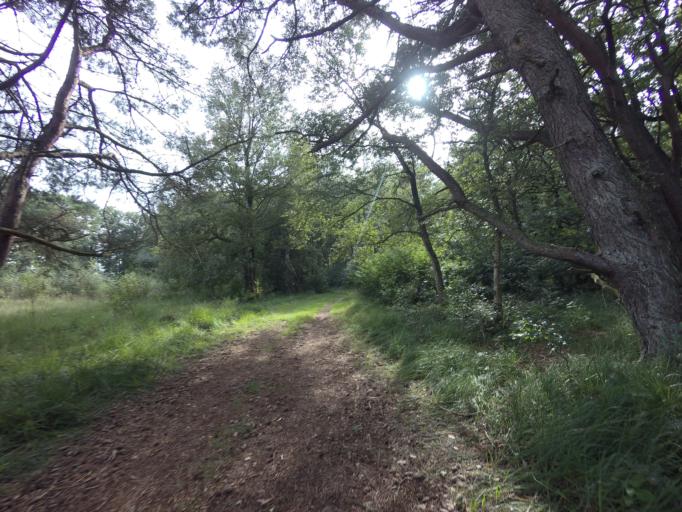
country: NL
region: Friesland
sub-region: Gemeente Heerenveen
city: Jubbega
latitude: 52.9618
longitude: 6.1397
